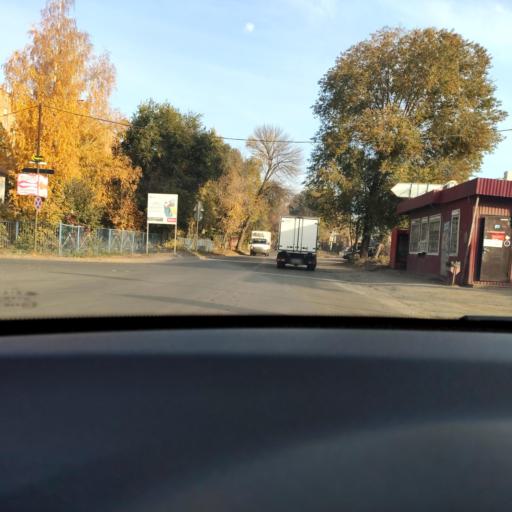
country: RU
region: Samara
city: Samara
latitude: 53.1882
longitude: 50.2450
